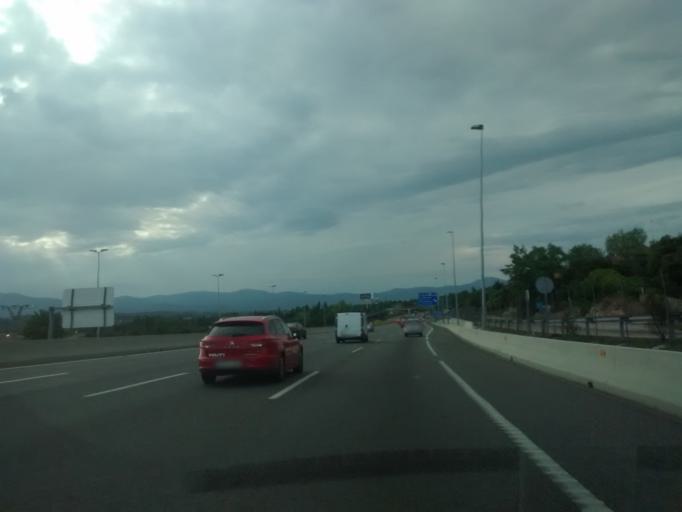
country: ES
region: Madrid
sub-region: Provincia de Madrid
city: Torrelodones
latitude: 40.5801
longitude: -3.9464
